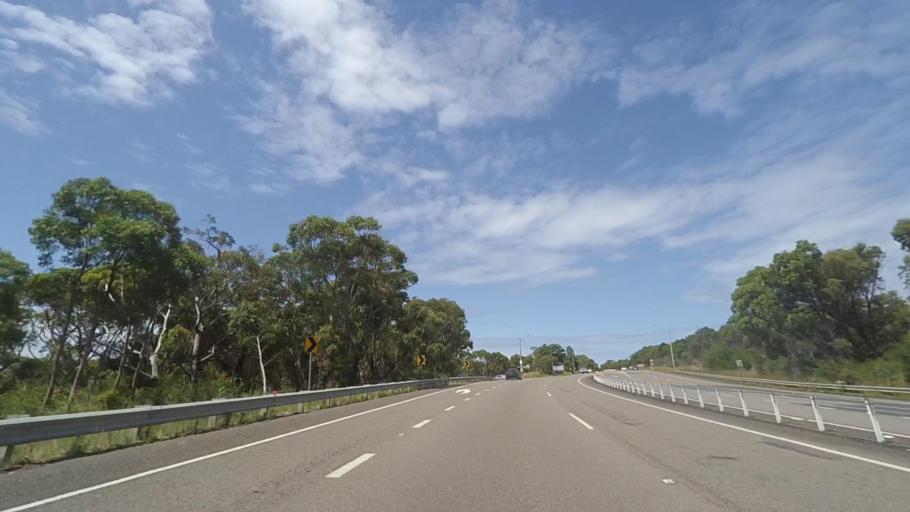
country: AU
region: New South Wales
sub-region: Wyong Shire
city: Kingfisher Shores
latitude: -33.1350
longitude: 151.6110
